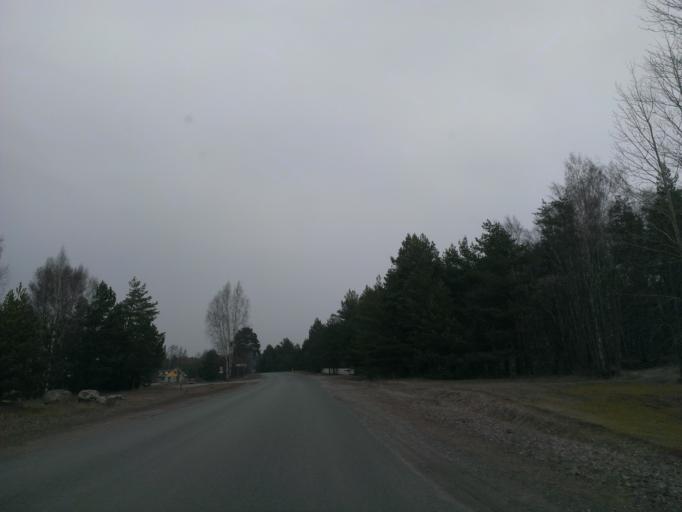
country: LV
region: Salacgrivas
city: Ainazi
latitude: 58.0104
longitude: 24.4486
